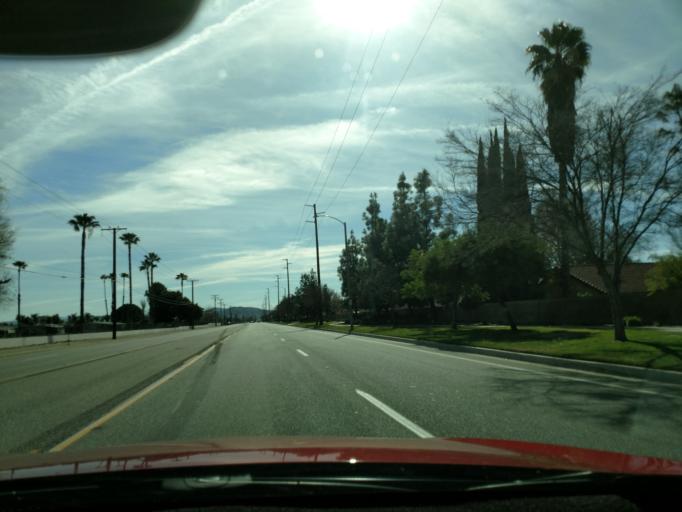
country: US
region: California
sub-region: Riverside County
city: Hemet
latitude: 33.7568
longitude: -117.0067
